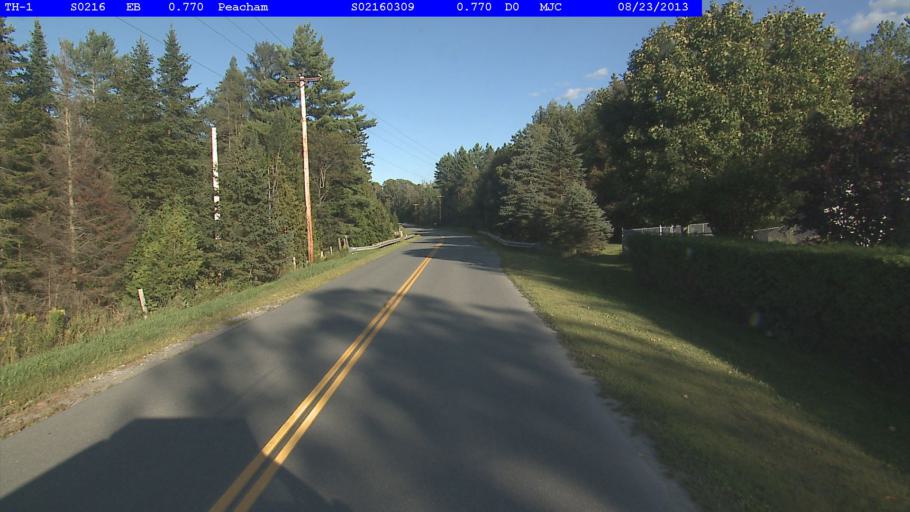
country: US
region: Vermont
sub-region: Caledonia County
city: Saint Johnsbury
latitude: 44.3091
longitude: -72.1535
